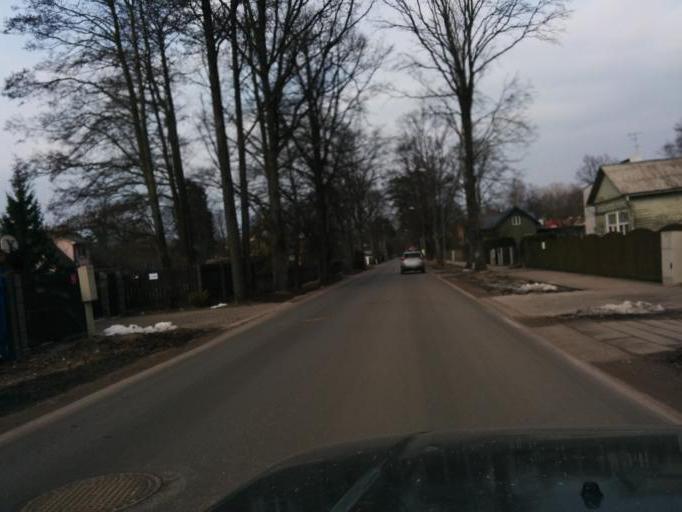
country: LV
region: Jurmala
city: Jurmala
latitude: 56.9598
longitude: 23.7227
